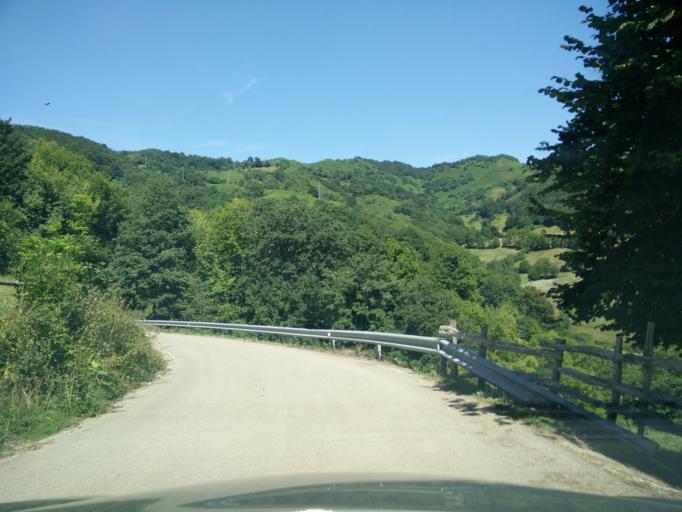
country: ES
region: Asturias
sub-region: Province of Asturias
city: Amieva
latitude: 43.1971
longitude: -5.1262
